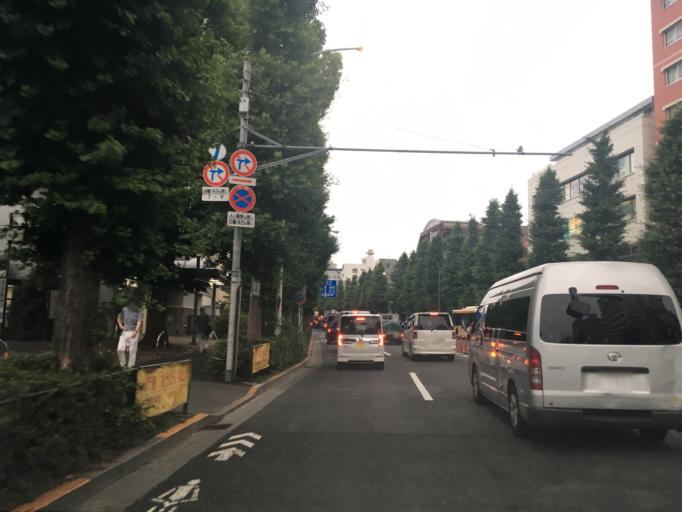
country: JP
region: Tokyo
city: Tokyo
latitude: 35.6980
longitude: 139.6581
